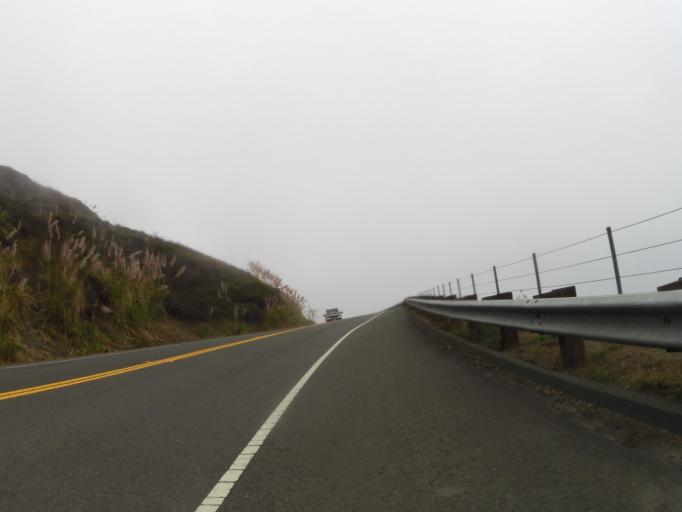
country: US
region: California
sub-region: Sonoma County
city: Monte Rio
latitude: 38.4840
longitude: -123.1763
